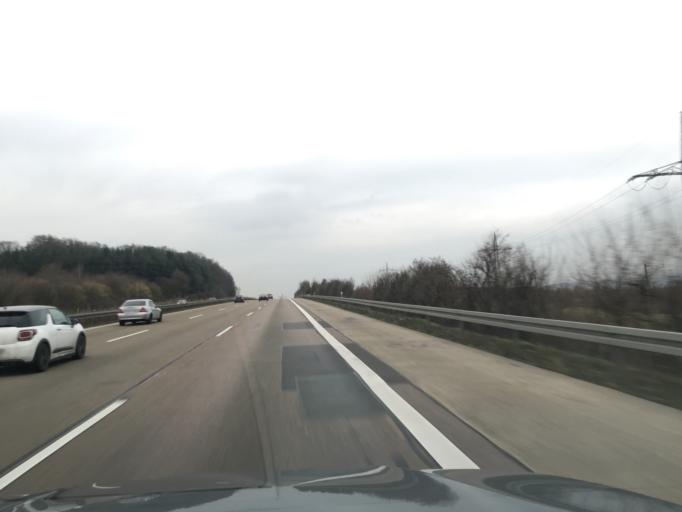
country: DE
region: Hesse
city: Bad Camberg
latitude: 50.3179
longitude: 8.2248
